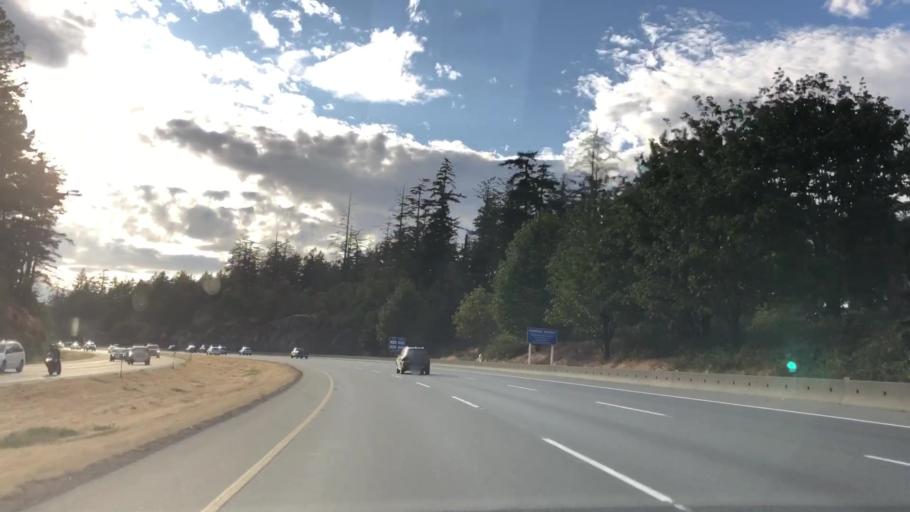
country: CA
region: British Columbia
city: Langford
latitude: 48.4650
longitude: -123.4774
